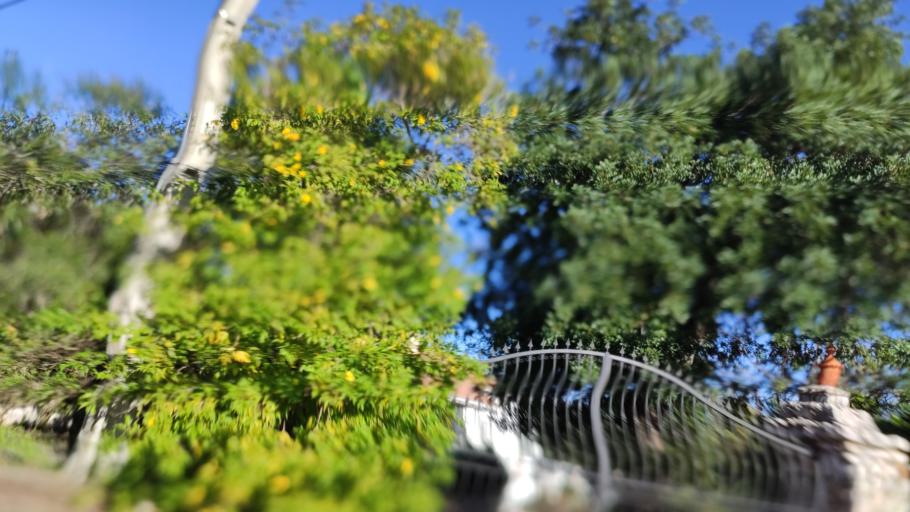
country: PT
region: Faro
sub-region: Sao Bras de Alportel
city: Sao Bras de Alportel
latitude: 37.1549
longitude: -7.9080
